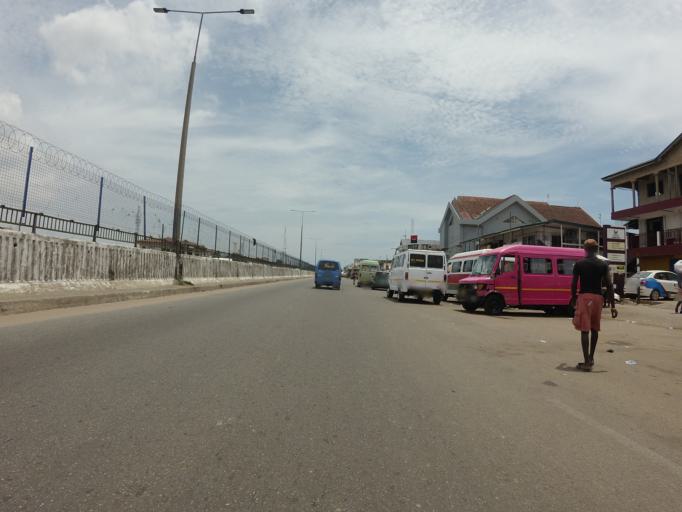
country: GH
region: Greater Accra
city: Accra
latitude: 5.5646
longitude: -0.2348
